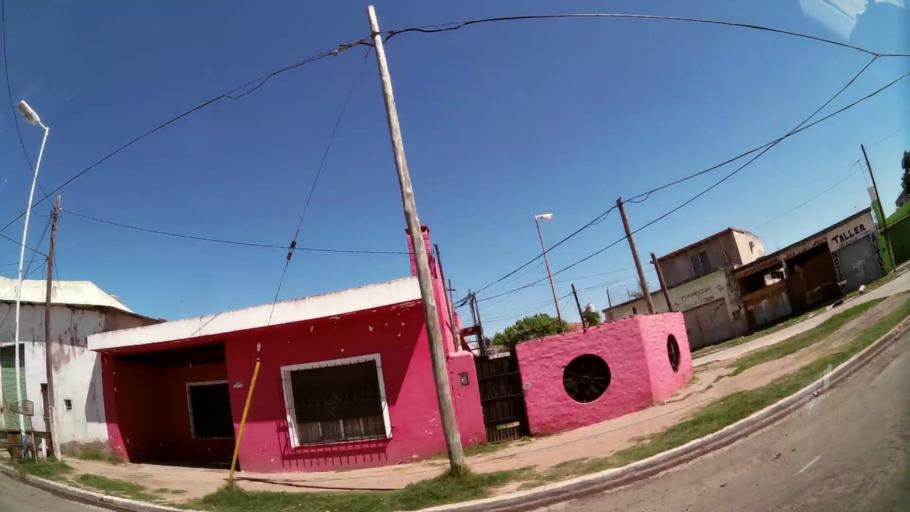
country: AR
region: Buenos Aires
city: Hurlingham
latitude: -34.5056
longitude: -58.6681
